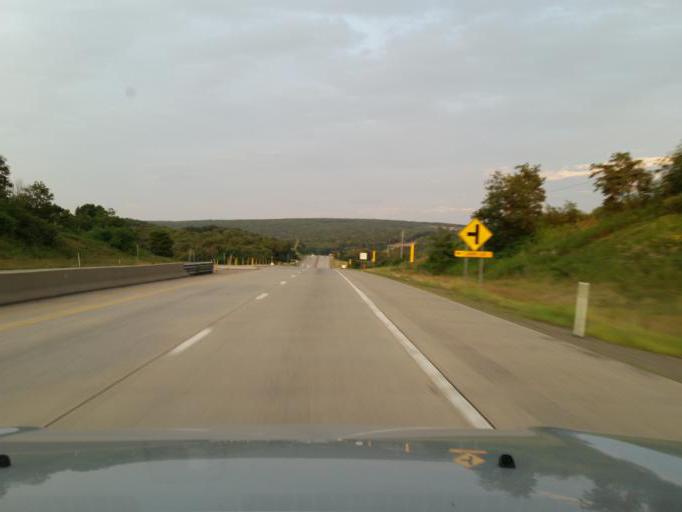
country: US
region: Pennsylvania
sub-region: Cambria County
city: Vinco
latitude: 40.4423
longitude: -78.9611
